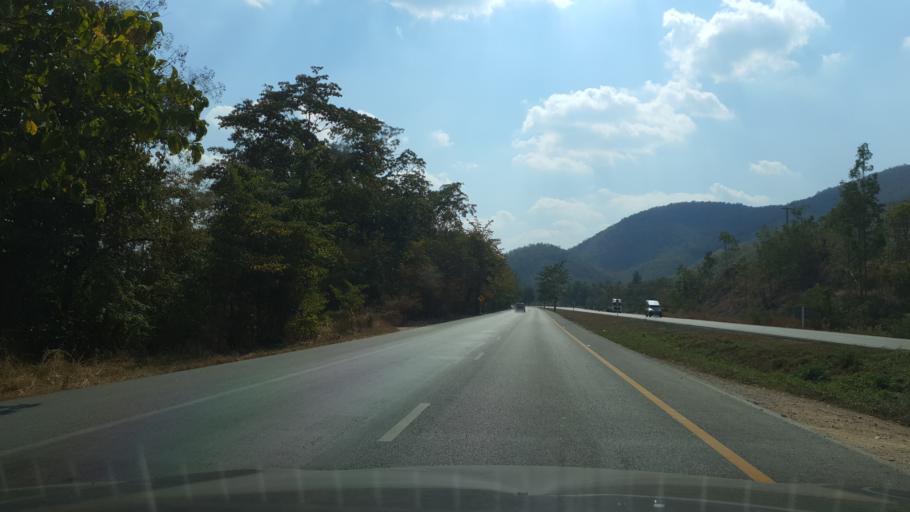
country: TH
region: Lampang
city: Mae Phrik
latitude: 17.3470
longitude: 99.1497
